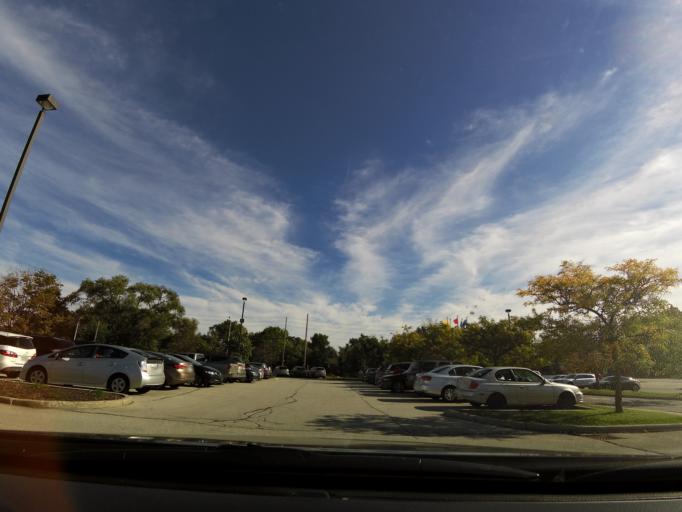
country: CA
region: Ontario
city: Burlington
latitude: 43.3266
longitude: -79.8284
